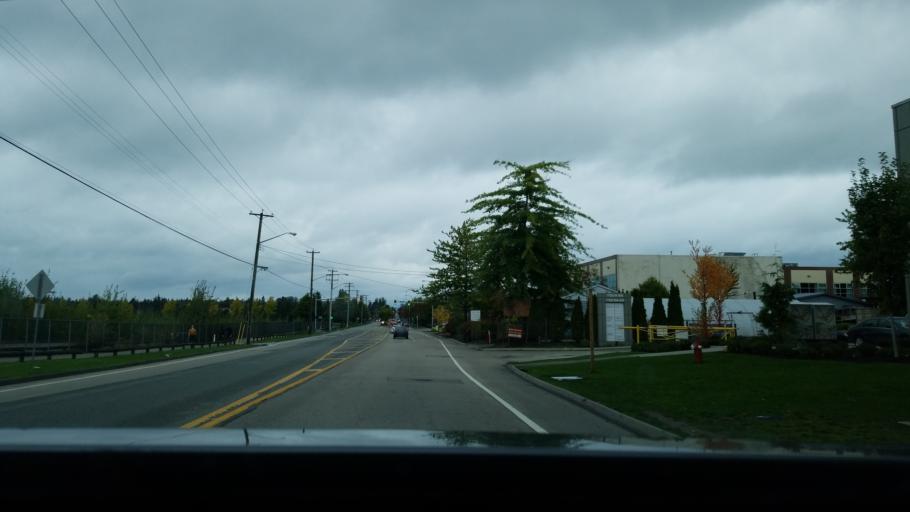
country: CA
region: British Columbia
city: Langley
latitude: 49.1188
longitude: -122.7284
